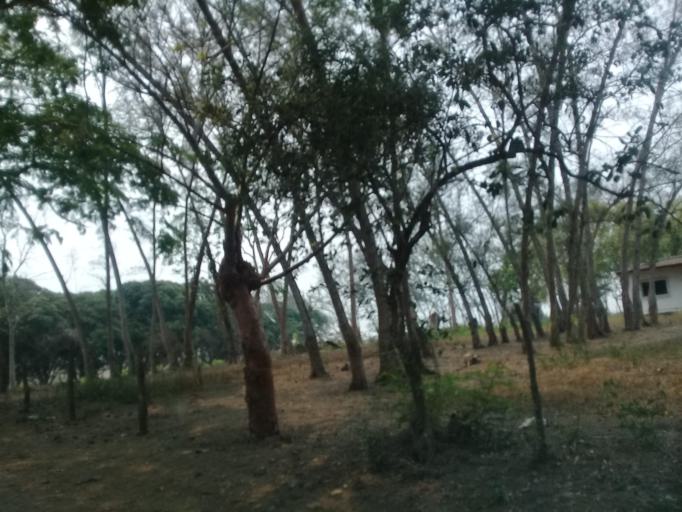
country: MX
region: Veracruz
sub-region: Medellin
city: La Laguna y Monte del Castillo
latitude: 18.9534
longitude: -96.1258
